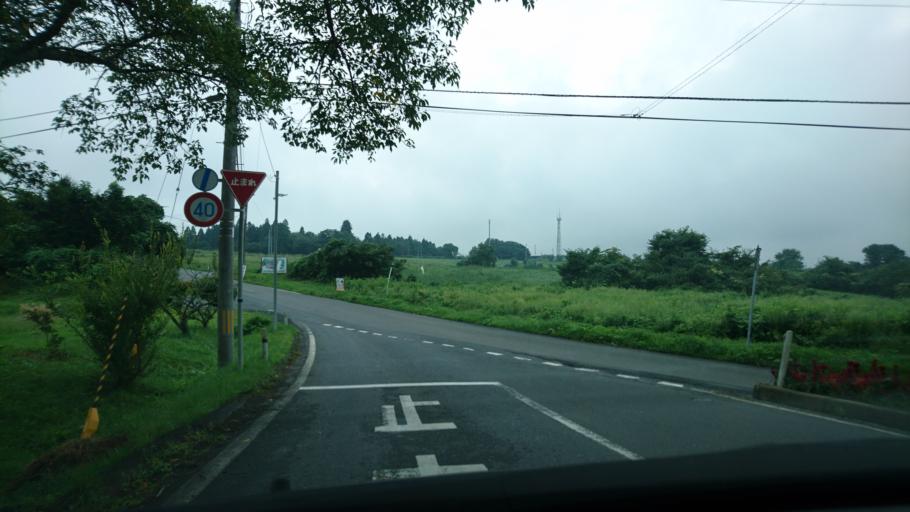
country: JP
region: Iwate
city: Ichinoseki
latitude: 38.9313
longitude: 141.1998
